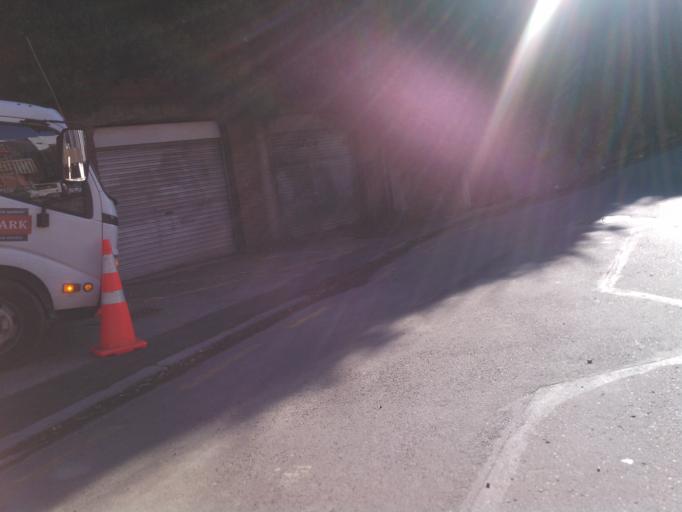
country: NZ
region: Wellington
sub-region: Wellington City
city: Kelburn
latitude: -41.2896
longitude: 174.7673
